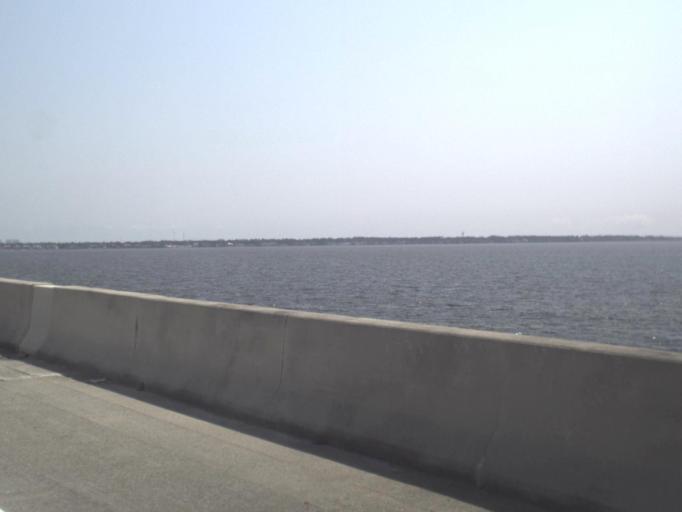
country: US
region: Florida
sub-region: Santa Rosa County
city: Oriole Beach
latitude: 30.4228
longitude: -87.0917
